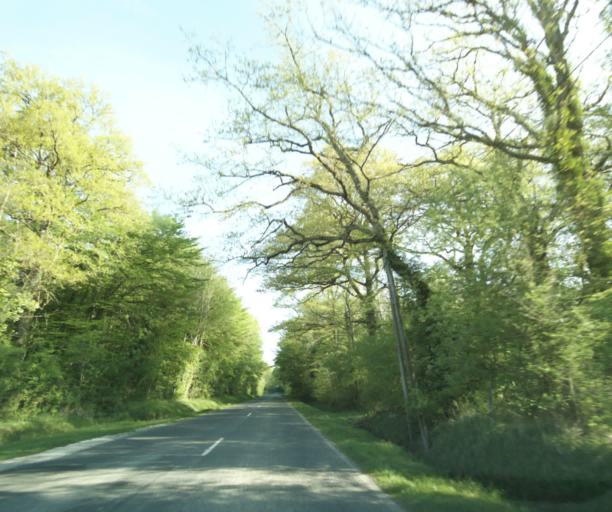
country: FR
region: Ile-de-France
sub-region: Departement de Seine-et-Marne
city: Vernou-la-Celle-sur-Seine
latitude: 48.4433
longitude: 2.8574
